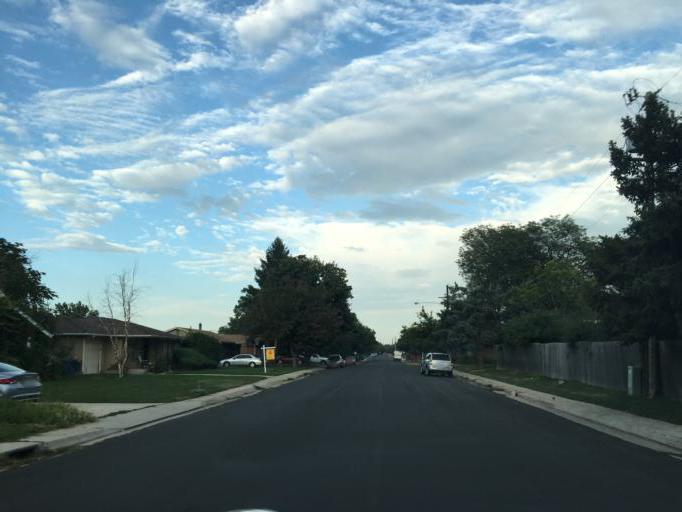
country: US
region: Colorado
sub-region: Adams County
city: Aurora
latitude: 39.7250
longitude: -104.8639
